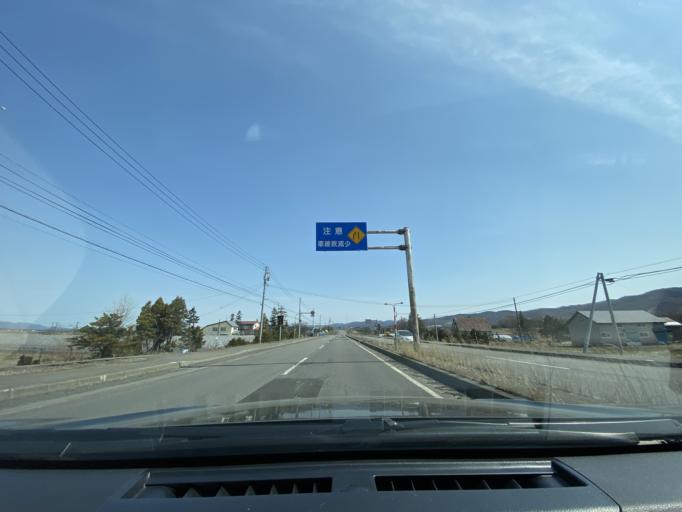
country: JP
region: Hokkaido
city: Bibai
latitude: 43.2873
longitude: 141.8411
